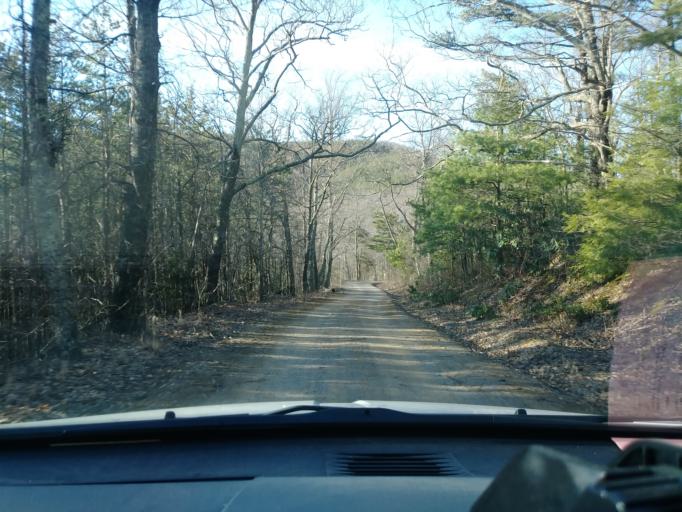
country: US
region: Tennessee
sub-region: Greene County
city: Tusculum
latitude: 36.0698
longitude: -82.6868
